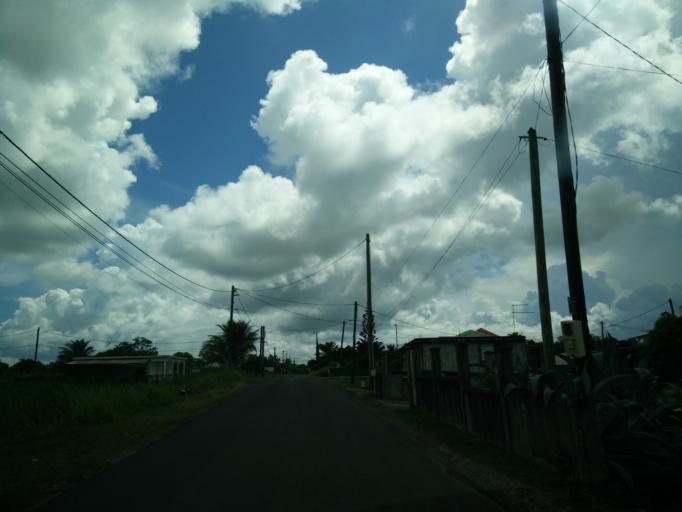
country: GP
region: Guadeloupe
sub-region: Guadeloupe
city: Le Moule
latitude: 16.2752
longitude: -61.3421
